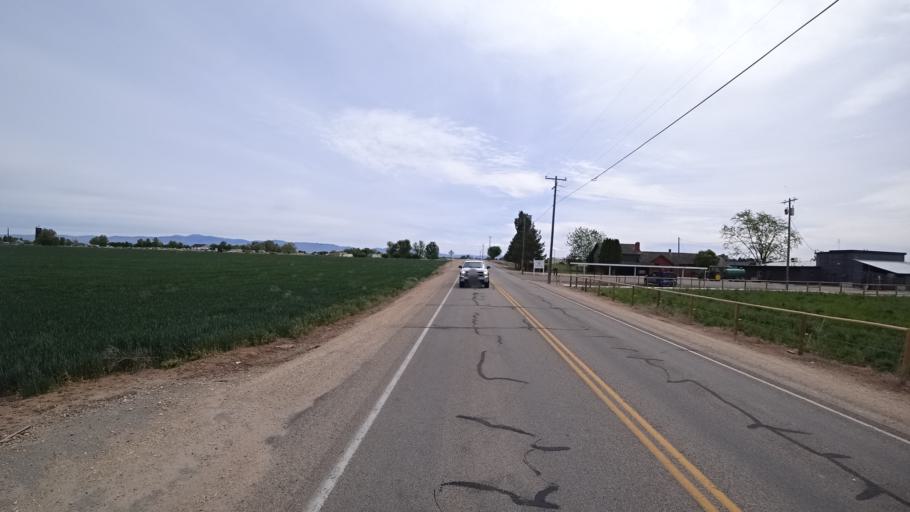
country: US
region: Idaho
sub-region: Ada County
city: Meridian
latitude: 43.5611
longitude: -116.4321
